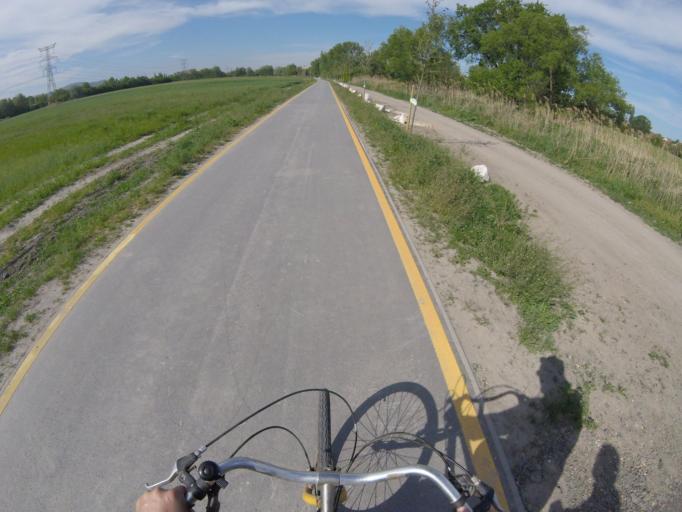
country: HU
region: Pest
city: Dunakeszi
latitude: 47.6332
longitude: 19.1211
